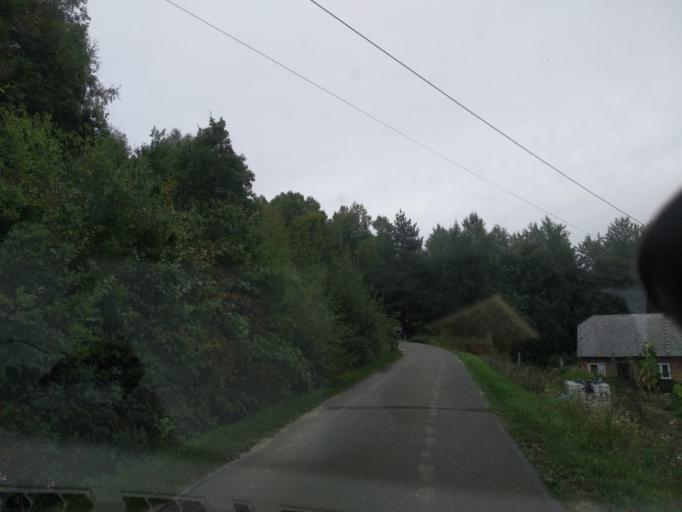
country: PL
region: Subcarpathian Voivodeship
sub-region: Powiat krosnienski
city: Korczyna
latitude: 49.7368
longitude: 21.8322
